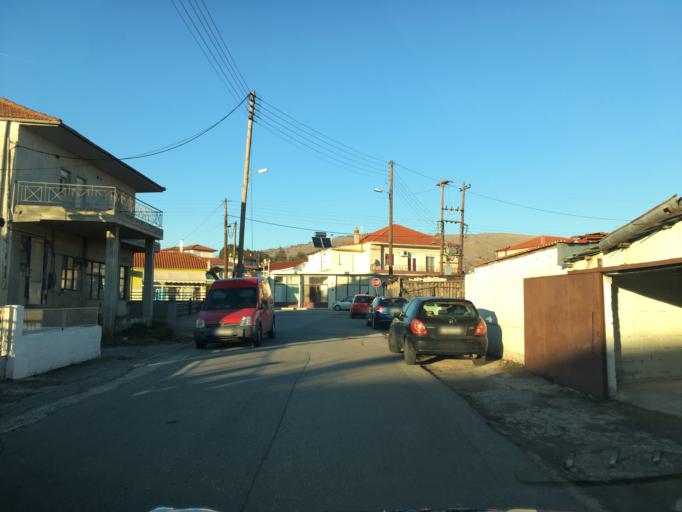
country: GR
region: West Macedonia
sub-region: Nomos Kozanis
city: Kozani
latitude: 40.2912
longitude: 21.7362
